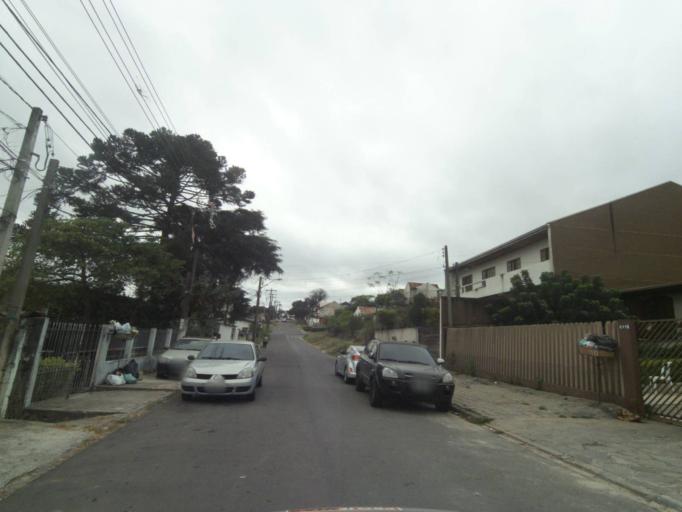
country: BR
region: Parana
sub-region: Sao Jose Dos Pinhais
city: Sao Jose dos Pinhais
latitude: -25.4877
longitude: -49.2297
